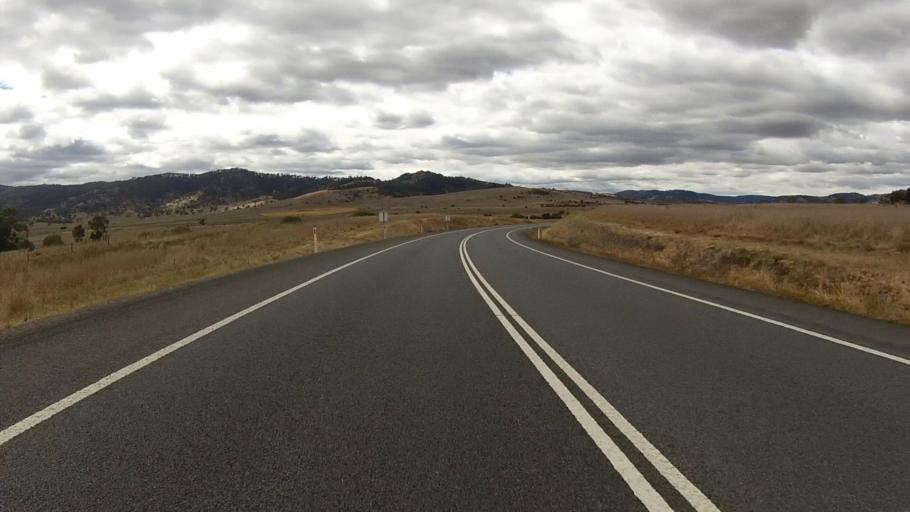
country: AU
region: Tasmania
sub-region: Brighton
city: Bridgewater
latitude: -42.6715
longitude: 147.2646
